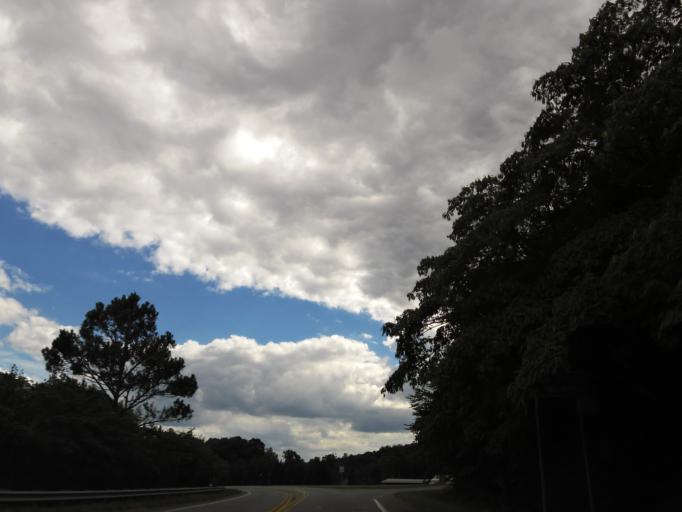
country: US
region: Tennessee
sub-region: Hamilton County
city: Lookout Mountain
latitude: 34.9820
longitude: -85.3343
